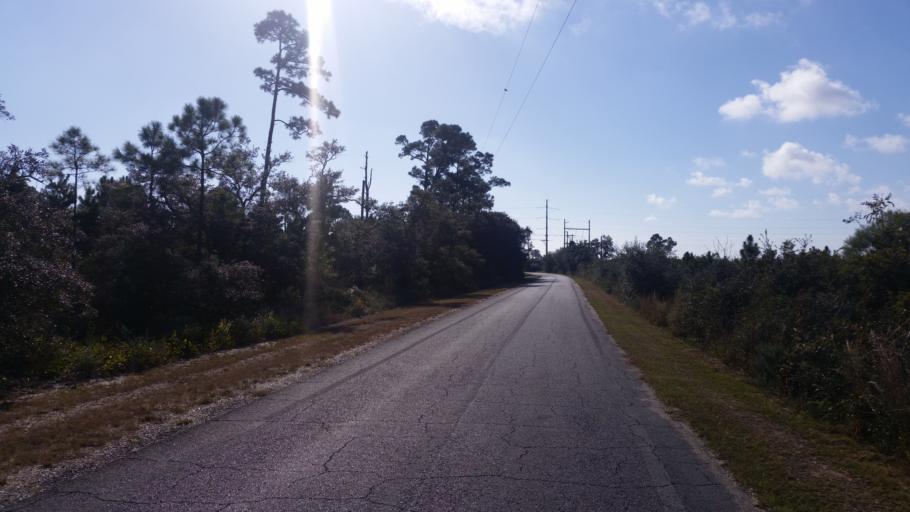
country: US
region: Alabama
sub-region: Baldwin County
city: Orange Beach
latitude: 30.2733
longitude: -87.6211
